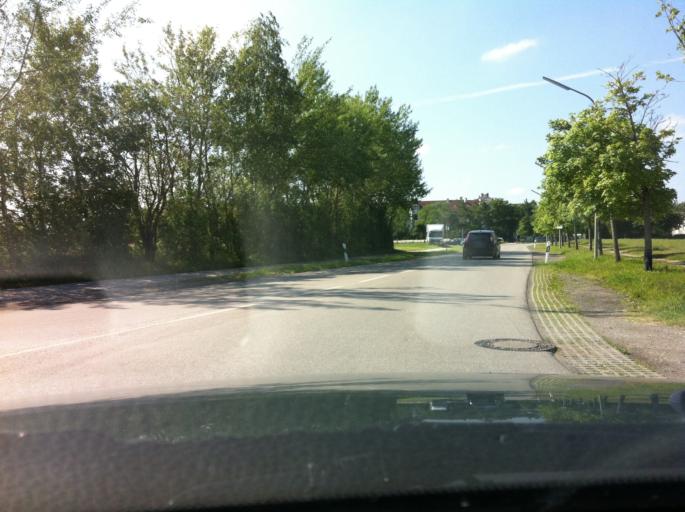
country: DE
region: Bavaria
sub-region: Upper Bavaria
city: Taufkirchen
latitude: 48.0539
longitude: 11.6158
